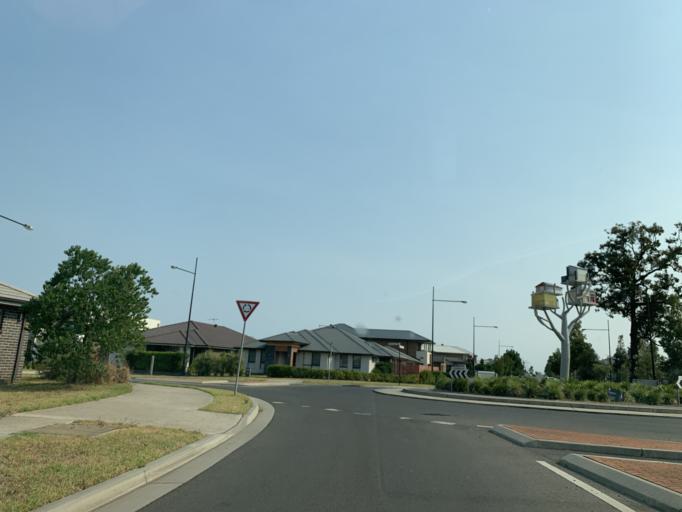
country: AU
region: New South Wales
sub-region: Blacktown
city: Stanhope Gardens
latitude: -33.7063
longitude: 150.9019
